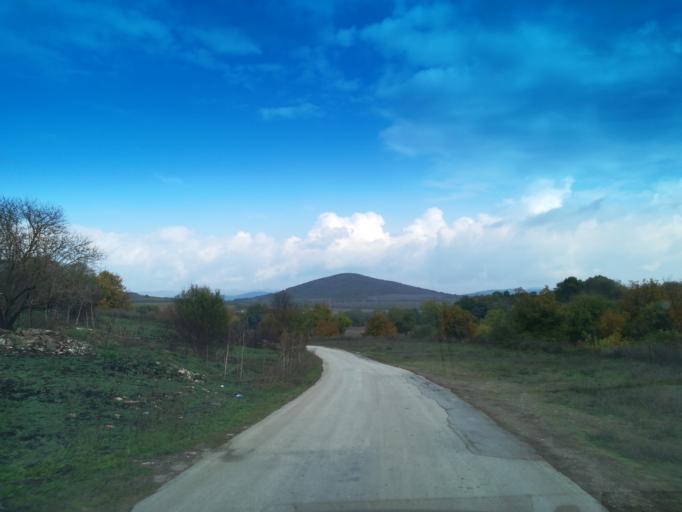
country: BG
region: Stara Zagora
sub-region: Obshtina Nikolaevo
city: Elkhovo
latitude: 42.3366
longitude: 25.4066
